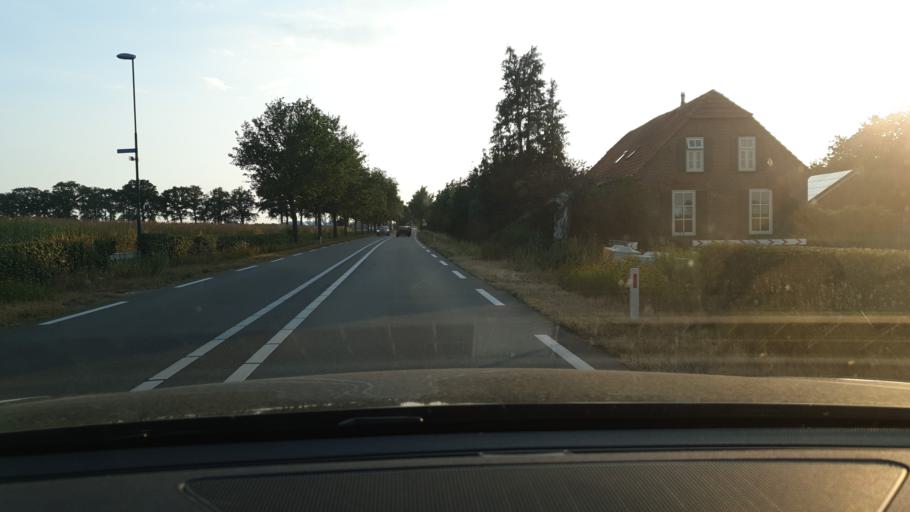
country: NL
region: North Brabant
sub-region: Gemeente Mill en Sint Hubert
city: Wilbertoord
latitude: 51.6678
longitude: 5.7578
